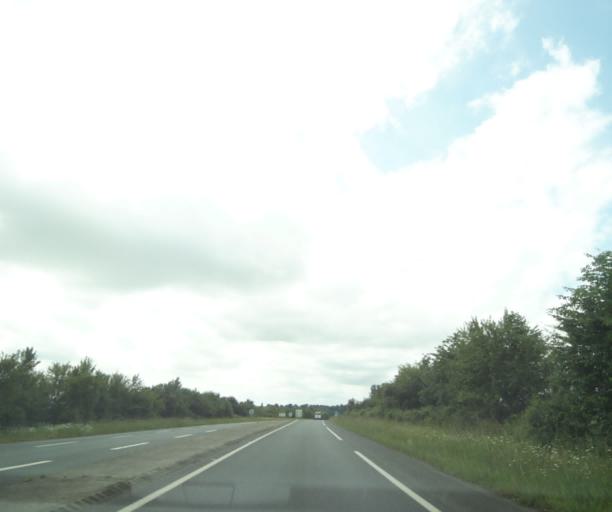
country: FR
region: Poitou-Charentes
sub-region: Departement des Deux-Sevres
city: Viennay
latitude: 46.7738
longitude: -0.2189
